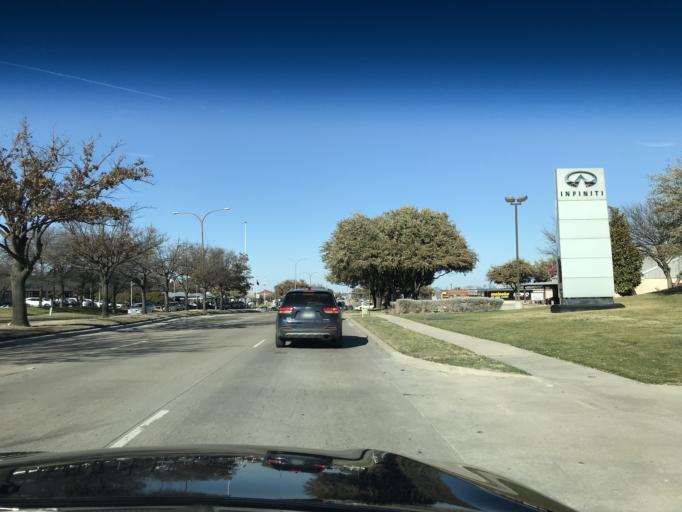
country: US
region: Texas
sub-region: Tarrant County
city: Benbrook
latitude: 32.6751
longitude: -97.4178
